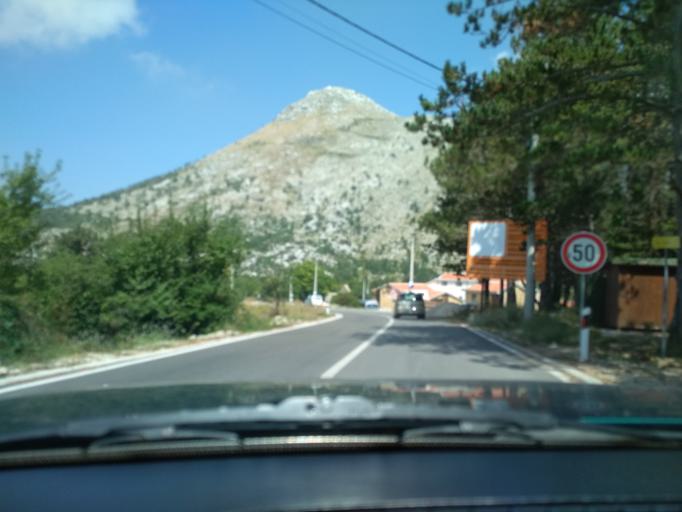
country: ME
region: Kotor
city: Kotor
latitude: 42.4259
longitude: 18.8002
